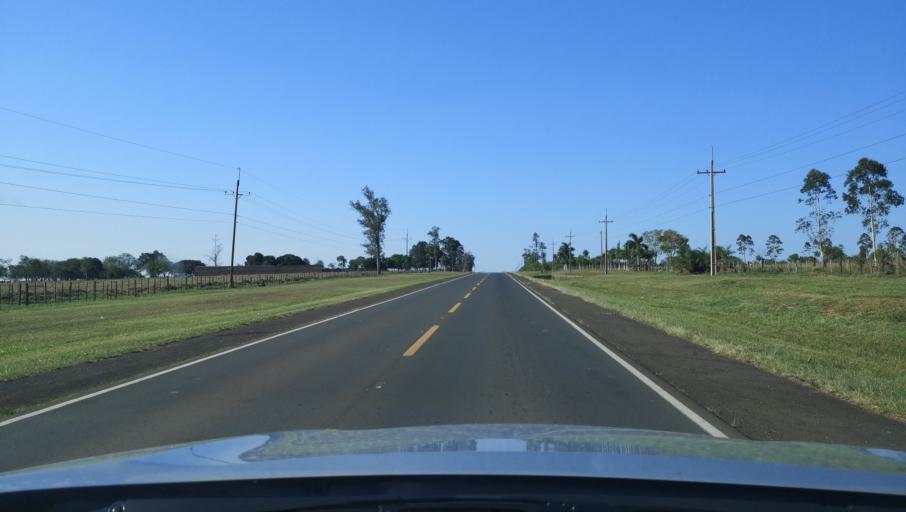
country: PY
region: Misiones
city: Santa Maria
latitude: -26.8268
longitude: -57.0293
